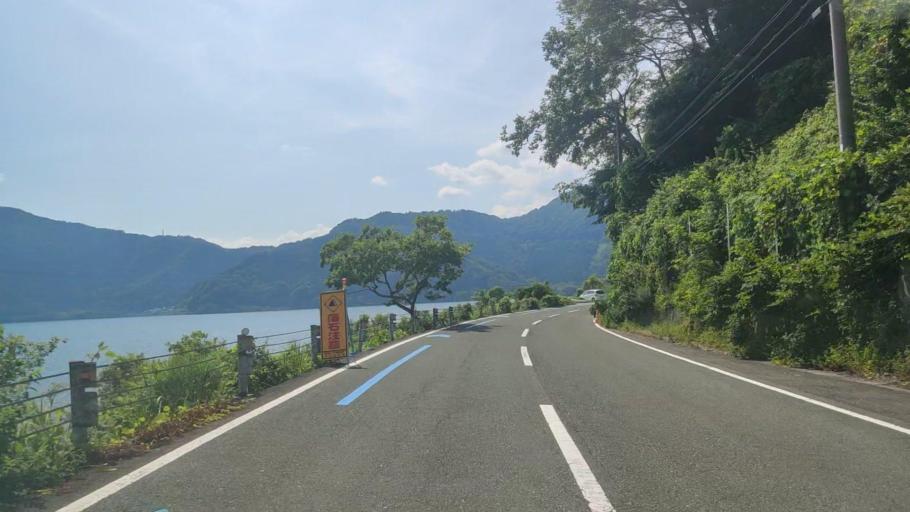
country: JP
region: Shiga Prefecture
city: Nagahama
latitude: 35.4990
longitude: 136.1751
